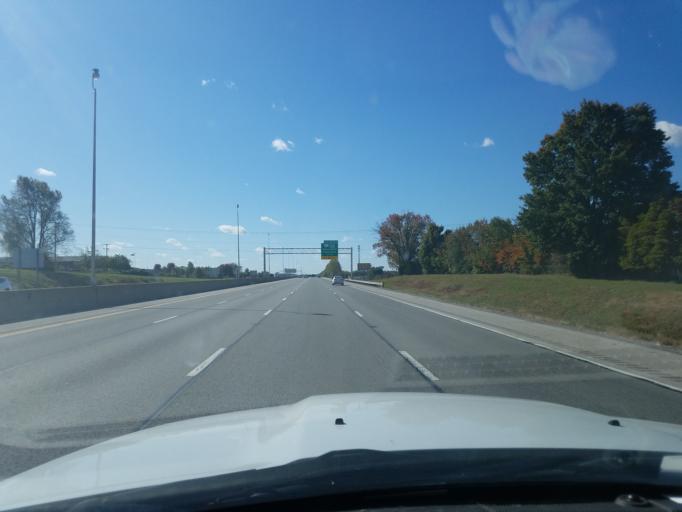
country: US
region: Kentucky
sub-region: Warren County
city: Plano
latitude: 36.9280
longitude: -86.4222
